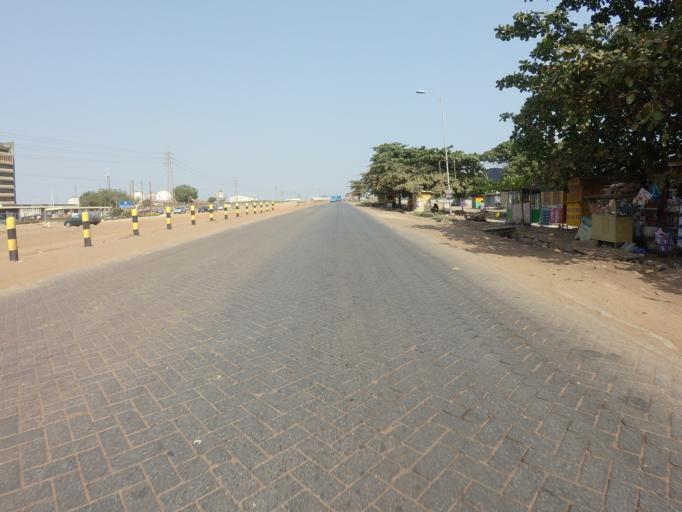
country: GH
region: Greater Accra
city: Tema
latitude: 5.6649
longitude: 0.0052
